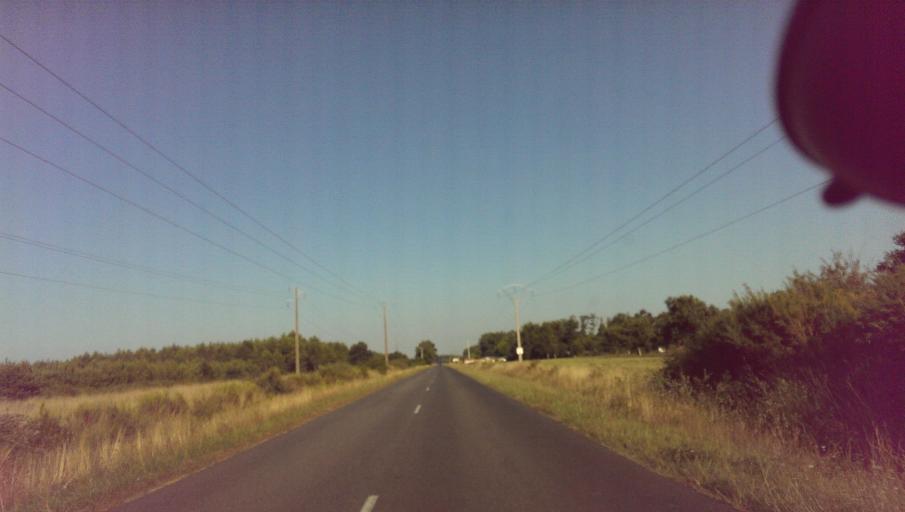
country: FR
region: Aquitaine
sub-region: Departement des Landes
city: Mimizan
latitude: 44.1833
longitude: -1.1857
